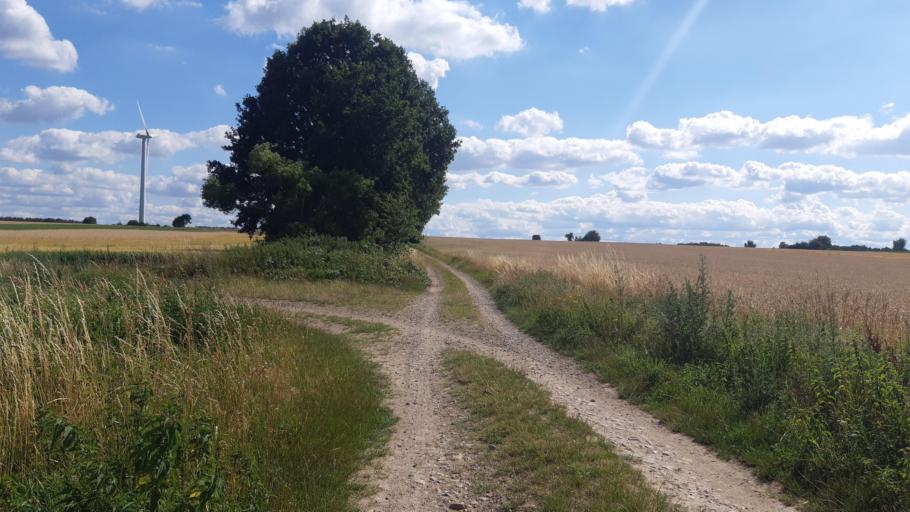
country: DE
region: Lower Saxony
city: Dahlem
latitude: 53.2097
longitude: 10.7584
